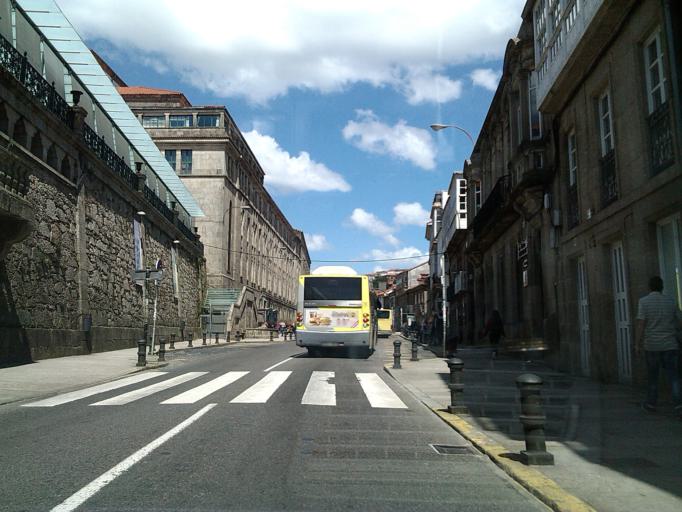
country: ES
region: Galicia
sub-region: Provincia da Coruna
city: Santiago de Compostela
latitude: 42.8799
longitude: -8.5408
